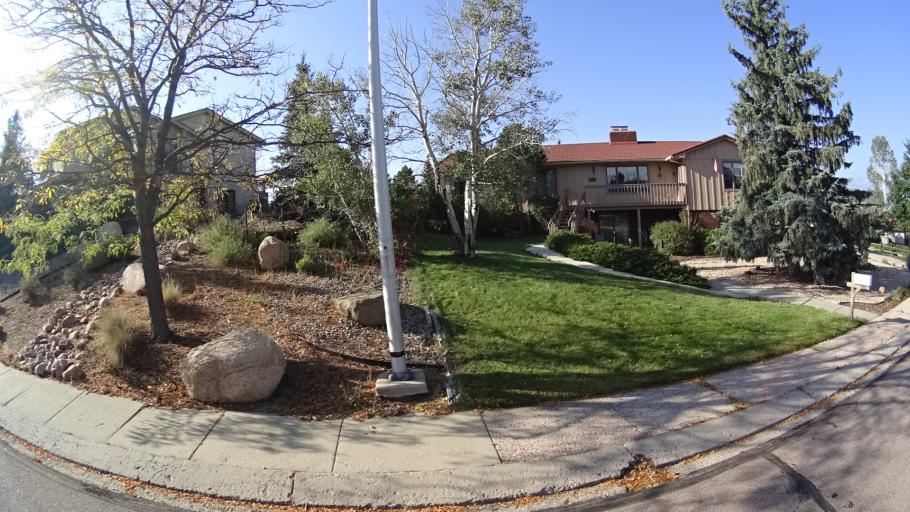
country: US
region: Colorado
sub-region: El Paso County
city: Cimarron Hills
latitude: 38.8936
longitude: -104.7288
